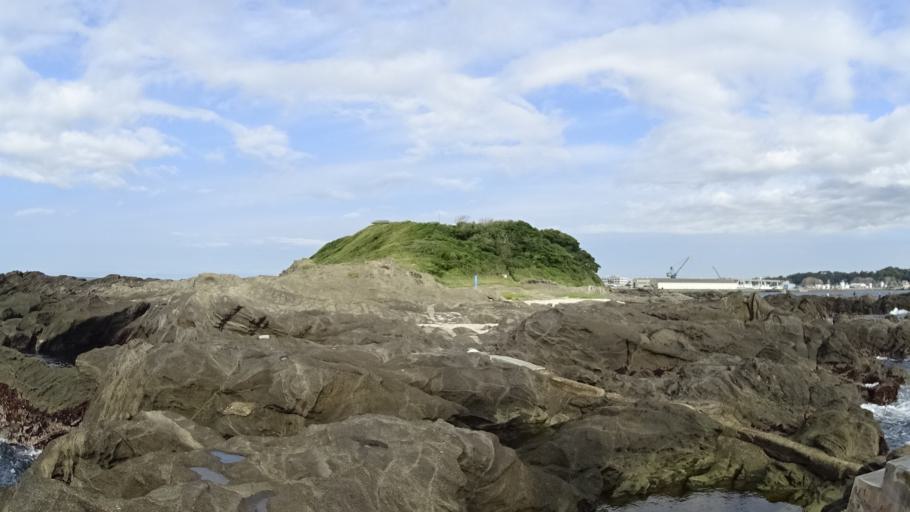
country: JP
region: Kanagawa
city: Miura
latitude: 35.1291
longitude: 139.6301
